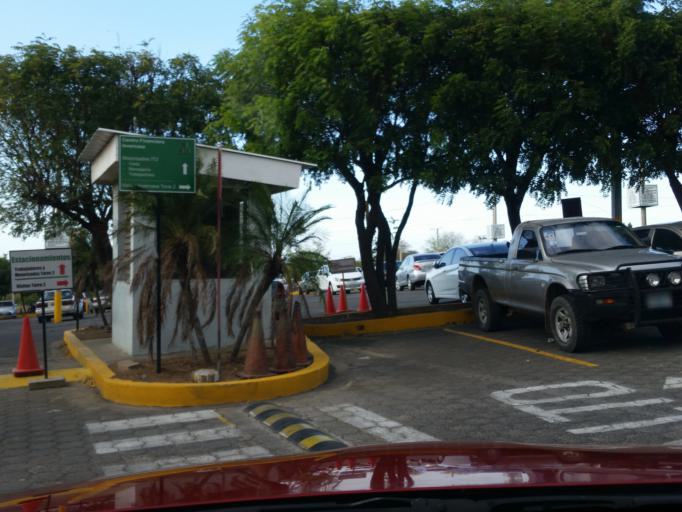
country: NI
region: Managua
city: Managua
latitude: 12.1138
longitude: -86.2666
